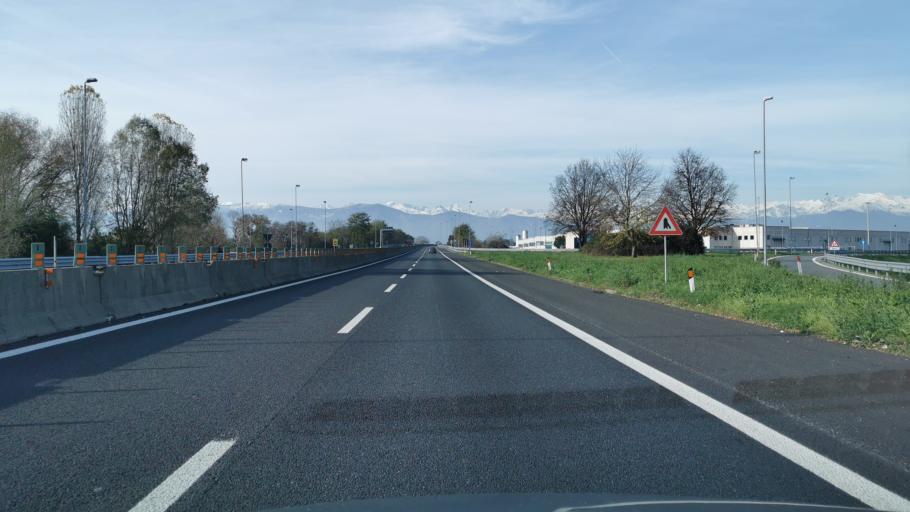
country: IT
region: Piedmont
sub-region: Provincia di Torino
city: Caselle Torinese
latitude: 45.1774
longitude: 7.6596
